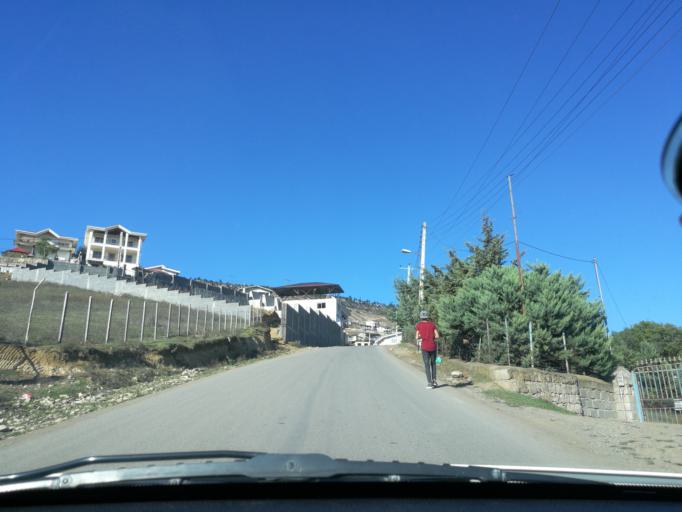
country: IR
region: Mazandaran
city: `Abbasabad
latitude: 36.5540
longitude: 51.1921
